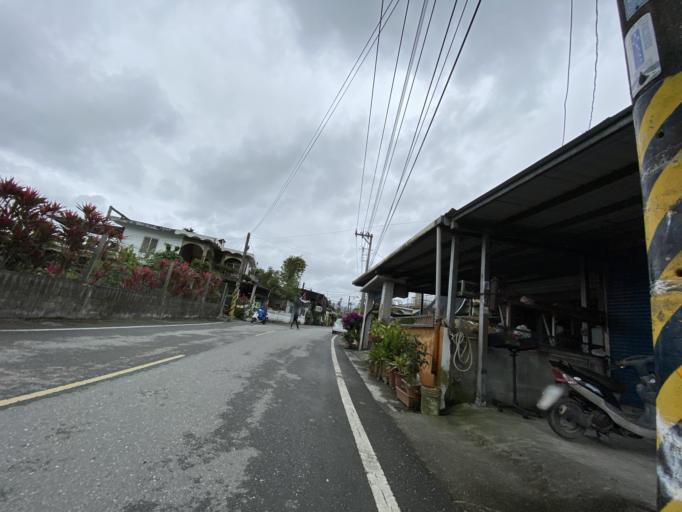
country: TW
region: Taiwan
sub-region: Hualien
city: Hualian
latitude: 23.6572
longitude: 121.4513
